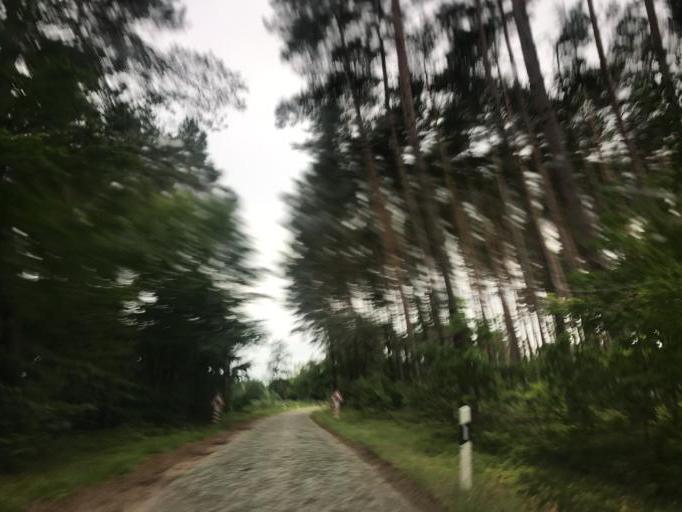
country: DE
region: Mecklenburg-Vorpommern
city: Wesenberg
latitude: 53.2839
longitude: 12.8859
